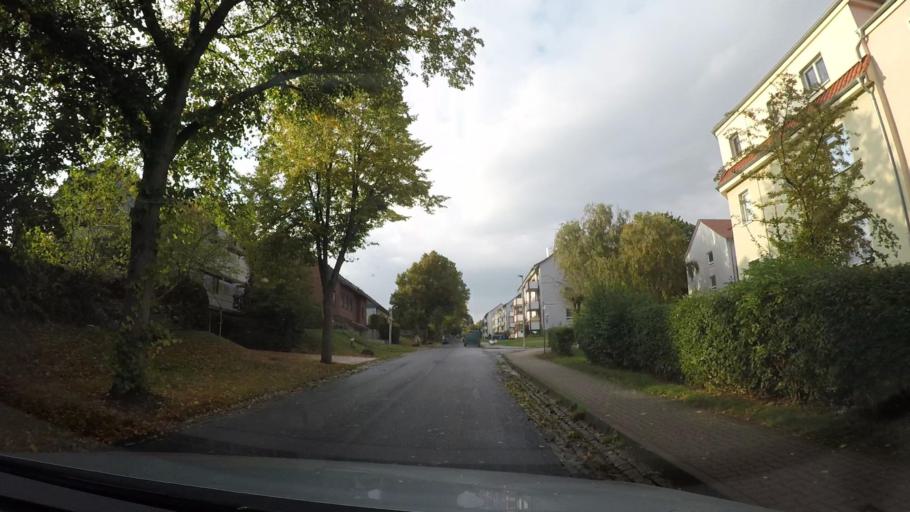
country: DE
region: Lower Saxony
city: Schoningen
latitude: 52.1342
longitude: 10.9622
